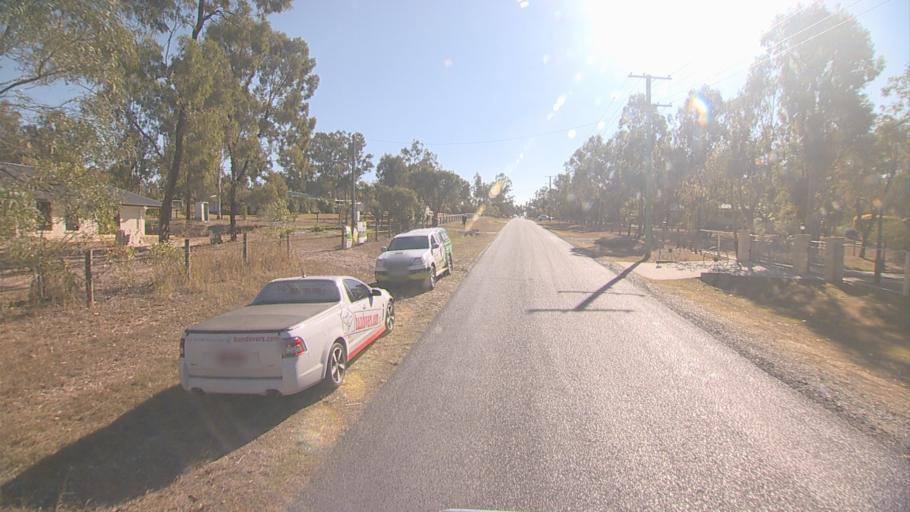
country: AU
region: Queensland
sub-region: Logan
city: Cedar Vale
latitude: -27.8389
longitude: 153.0314
